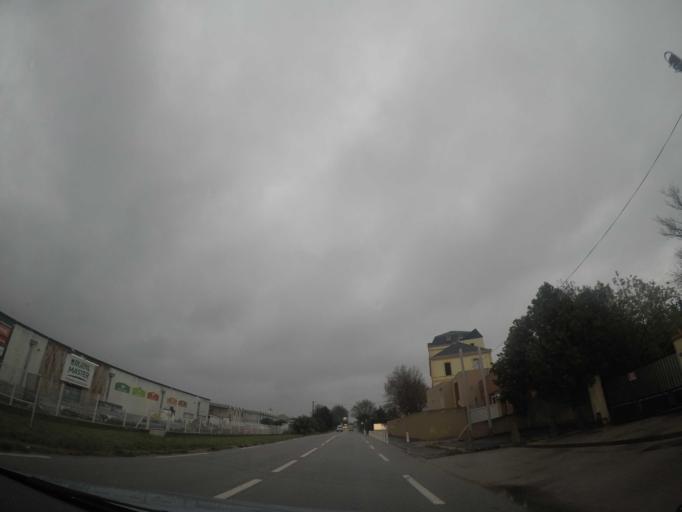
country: FR
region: Languedoc-Roussillon
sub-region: Departement des Pyrenees-Orientales
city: Baho
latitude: 42.6871
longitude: 2.8204
